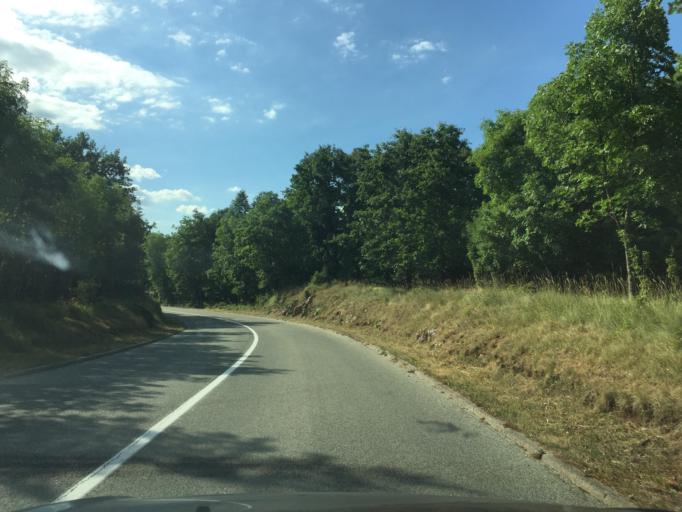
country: HR
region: Primorsko-Goranska
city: Klana
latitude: 45.4511
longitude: 14.3212
